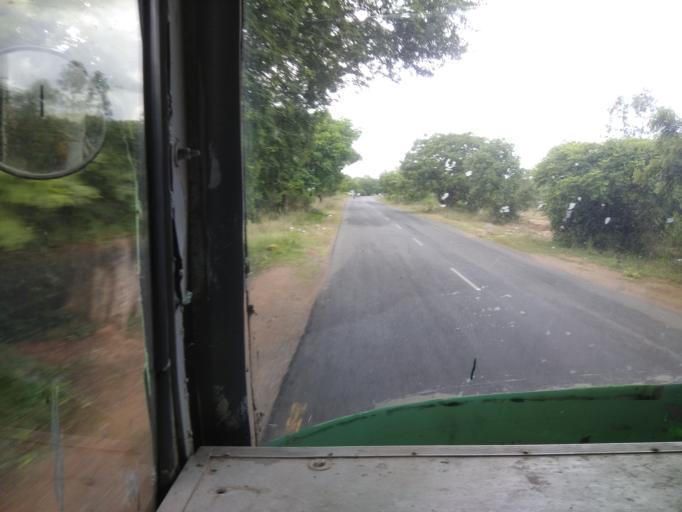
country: IN
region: Tamil Nadu
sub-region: Kancheepuram
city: Madurantakam
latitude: 12.4463
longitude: 79.8088
